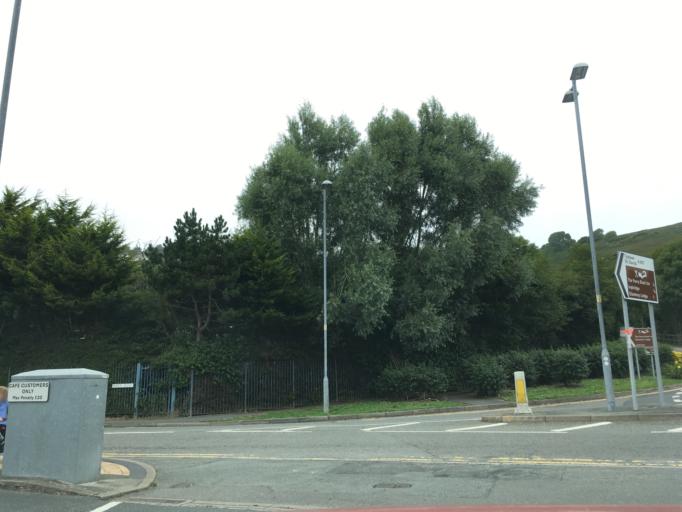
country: GB
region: Wales
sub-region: Pembrokeshire
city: Goodwick
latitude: 52.0030
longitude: -4.9935
